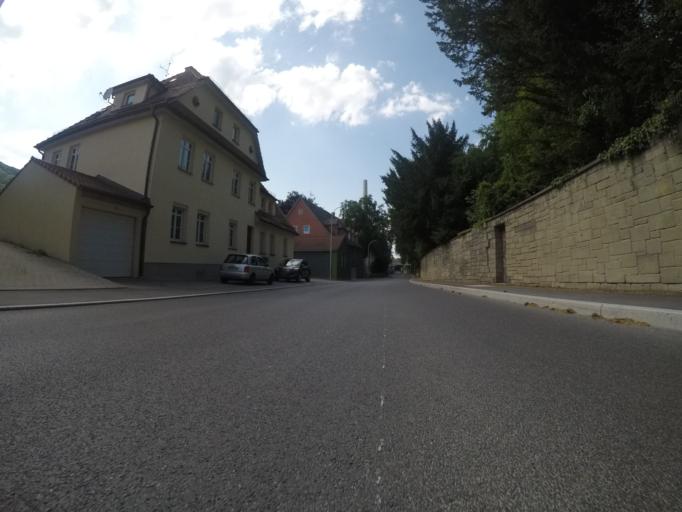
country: DE
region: Baden-Wuerttemberg
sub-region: Tuebingen Region
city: Grabenstetten
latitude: 48.5525
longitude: 9.4709
